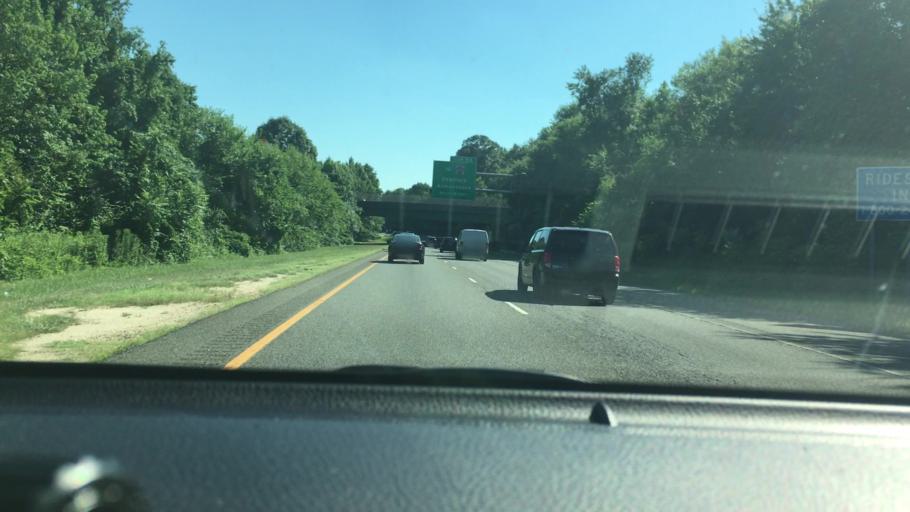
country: US
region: New Jersey
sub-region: Camden County
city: Glendora
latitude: 39.8374
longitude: -75.1002
